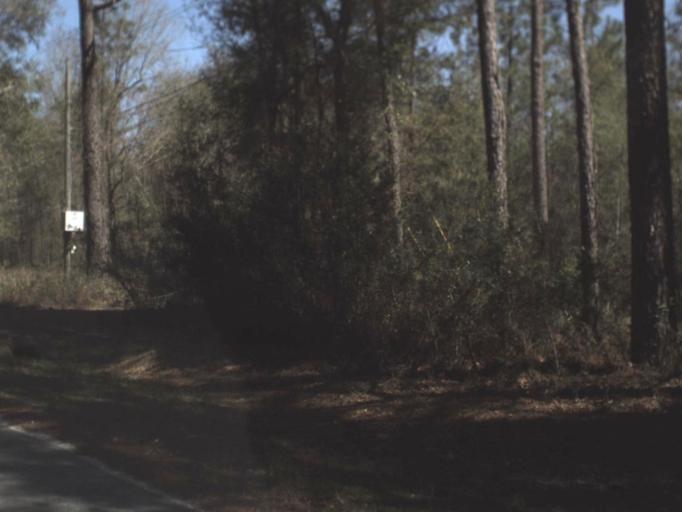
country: US
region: Florida
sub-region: Leon County
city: Woodville
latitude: 30.3121
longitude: -84.3117
